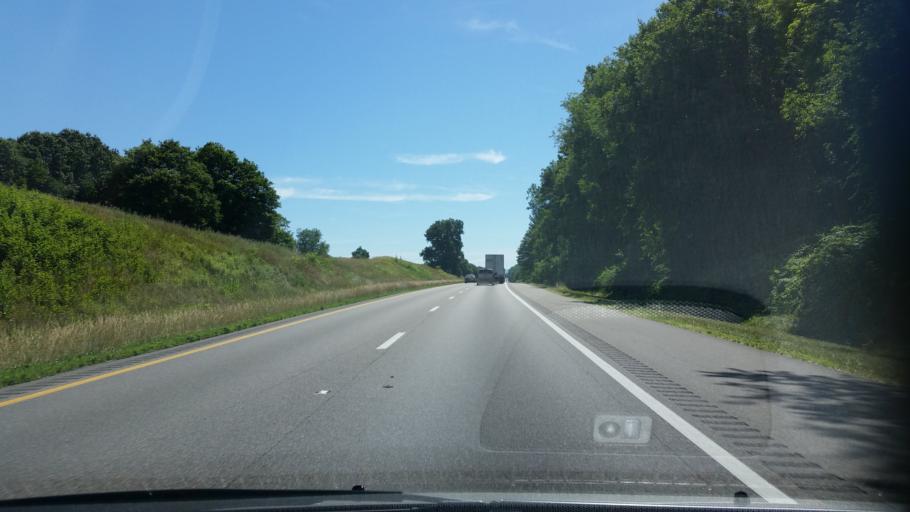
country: US
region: Virginia
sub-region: Washington County
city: Emory
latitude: 36.7686
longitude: -81.8189
